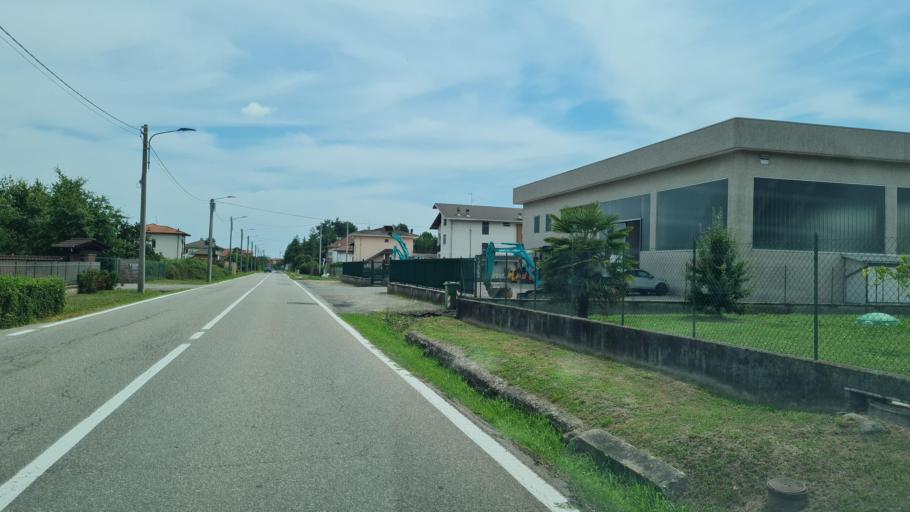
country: IT
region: Piedmont
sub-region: Provincia di Biella
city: Castelletto Cervo
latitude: 45.5448
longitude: 8.2129
